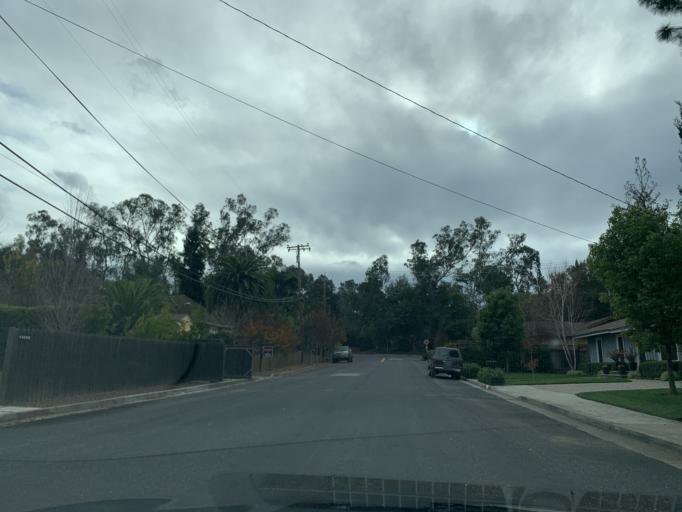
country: US
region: California
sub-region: Santa Clara County
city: Monte Sereno
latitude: 37.2611
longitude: -121.9767
